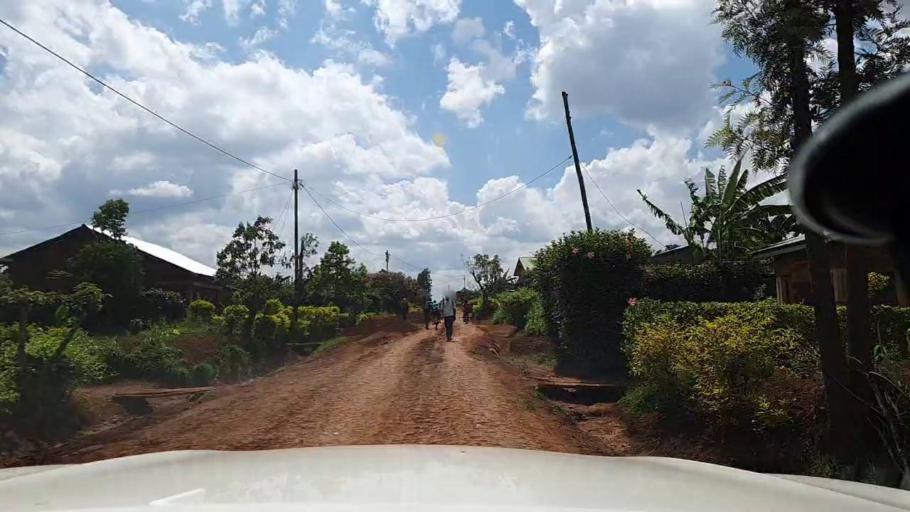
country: RW
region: Kigali
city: Kigali
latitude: -1.8336
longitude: 29.8365
